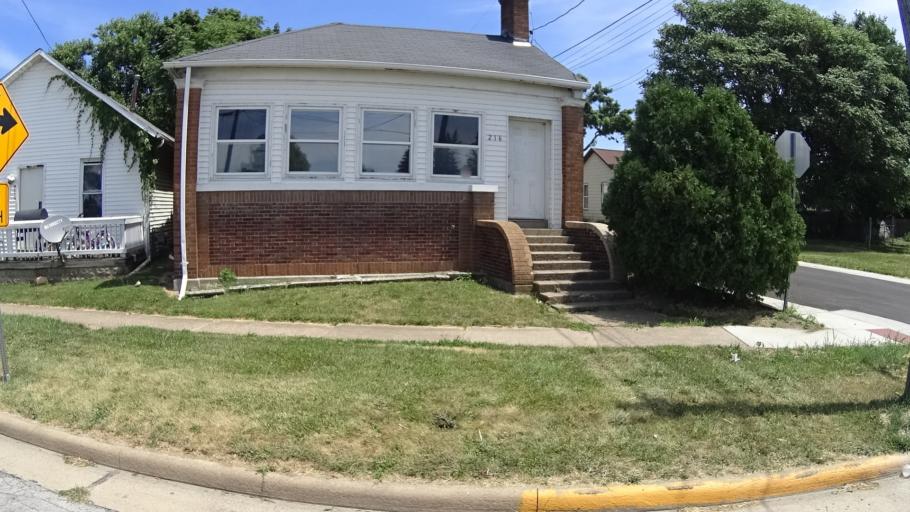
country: US
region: Ohio
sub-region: Erie County
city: Sandusky
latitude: 41.4520
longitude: -82.7221
